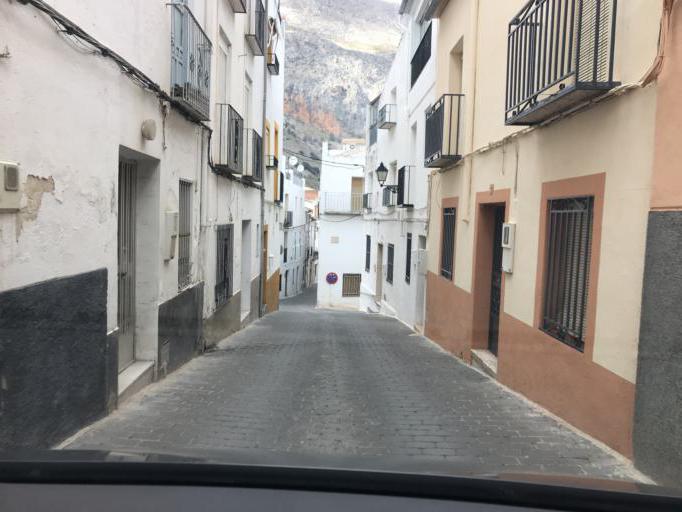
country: ES
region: Andalusia
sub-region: Provincia de Jaen
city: Torres
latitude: 37.7912
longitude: -3.4655
